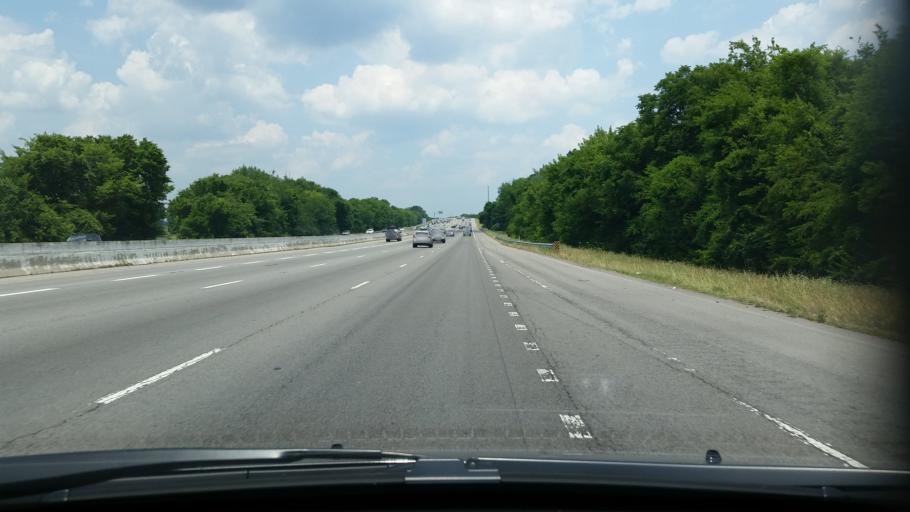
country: US
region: Tennessee
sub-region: Williamson County
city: Brentwood Estates
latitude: 36.0018
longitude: -86.7931
